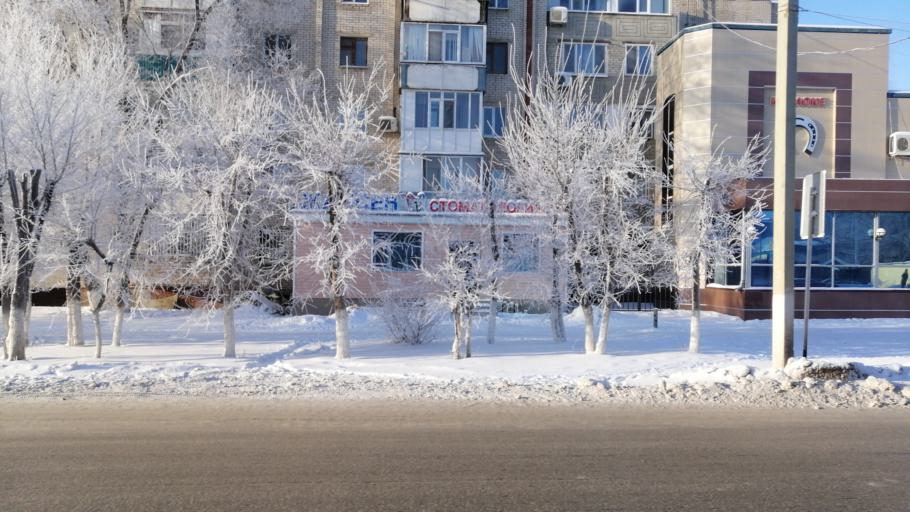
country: KZ
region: Aqtoebe
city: Aqtobe
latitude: 50.2964
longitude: 57.1466
